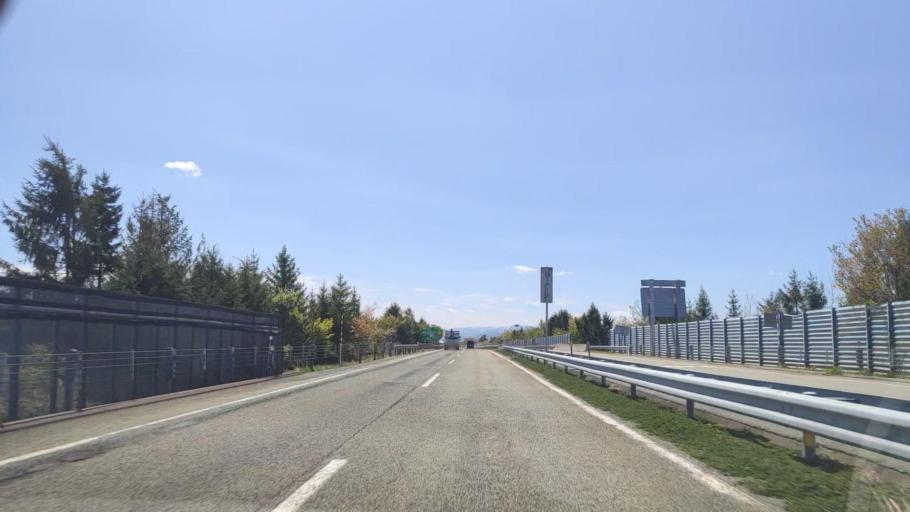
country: JP
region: Akita
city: Yokotemachi
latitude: 39.3159
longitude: 140.5157
